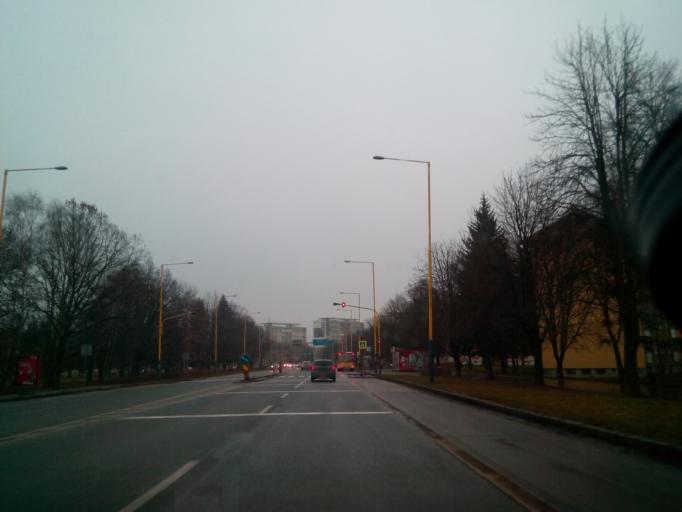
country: SK
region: Presovsky
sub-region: Okres Presov
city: Presov
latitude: 49.0010
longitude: 21.2228
